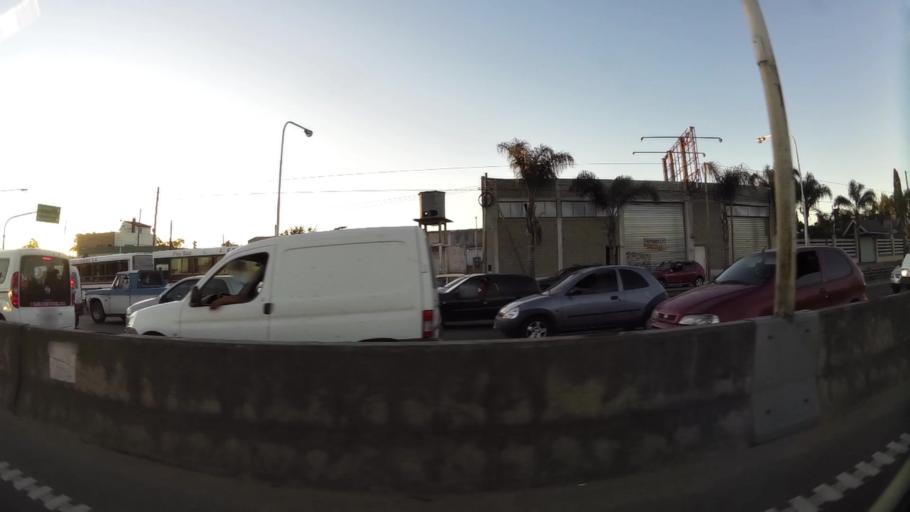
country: AR
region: Buenos Aires
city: Pontevedra
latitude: -34.7927
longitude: -58.6315
